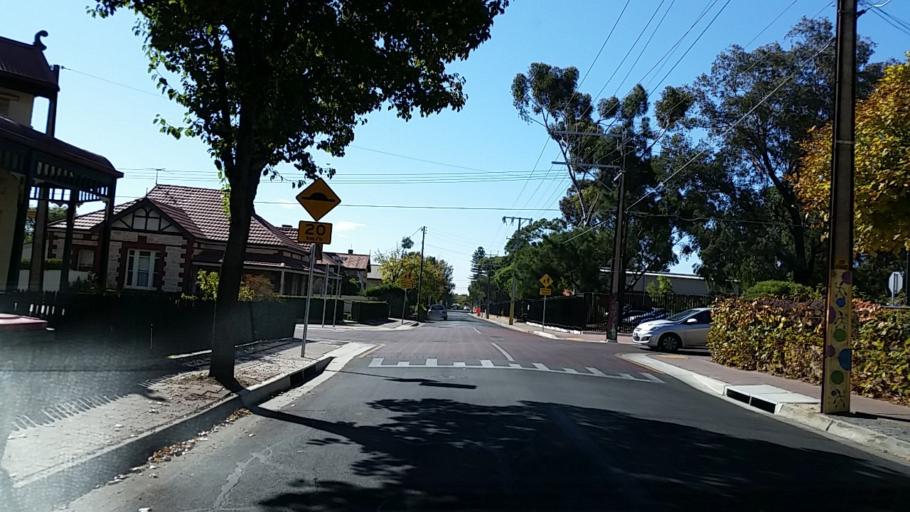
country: AU
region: South Australia
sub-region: Prospect
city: Prospect
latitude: -34.8860
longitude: 138.5894
